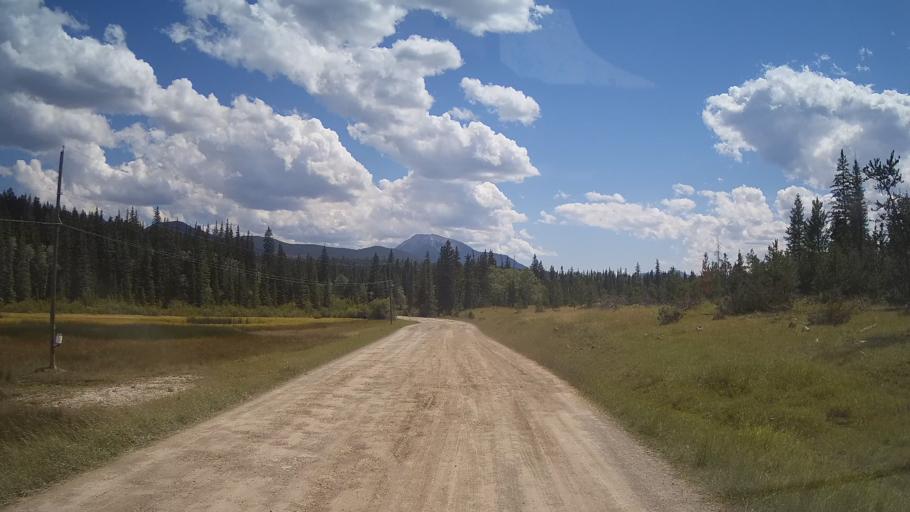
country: CA
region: British Columbia
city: Lillooet
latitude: 51.2946
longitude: -121.9806
